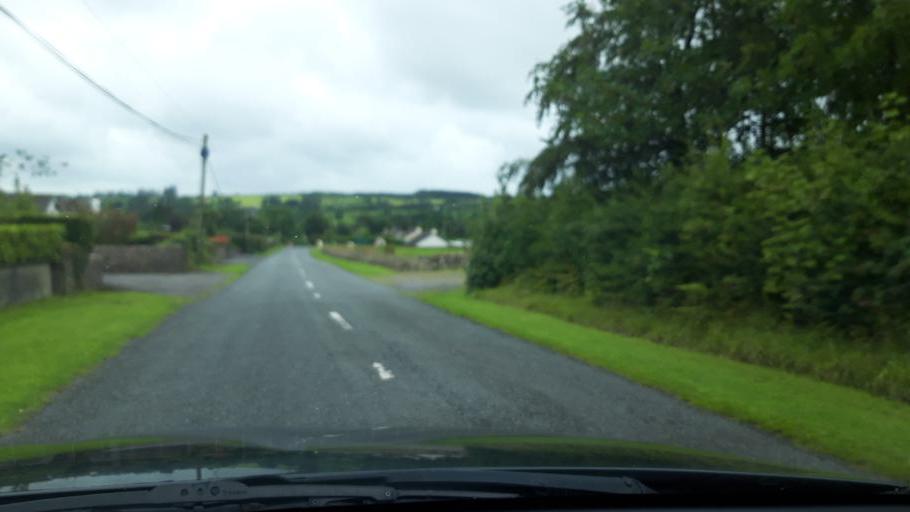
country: IE
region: Munster
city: Cahir
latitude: 52.1772
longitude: -7.8501
